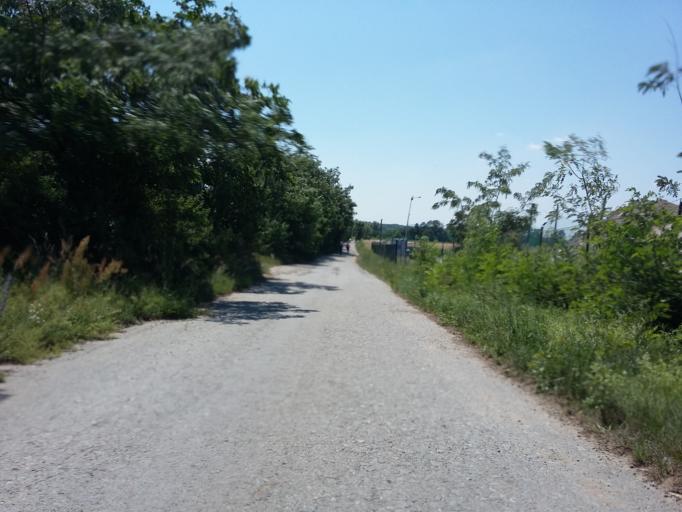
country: AT
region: Lower Austria
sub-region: Politischer Bezirk Ganserndorf
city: Marchegg
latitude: 48.2897
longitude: 16.9678
